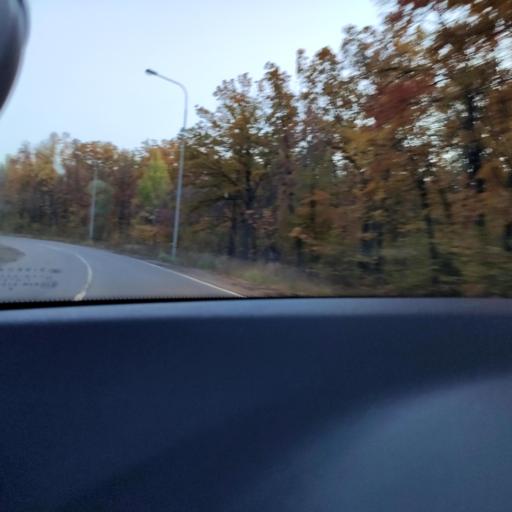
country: RU
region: Samara
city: Novosemeykino
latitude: 53.3822
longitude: 50.3118
